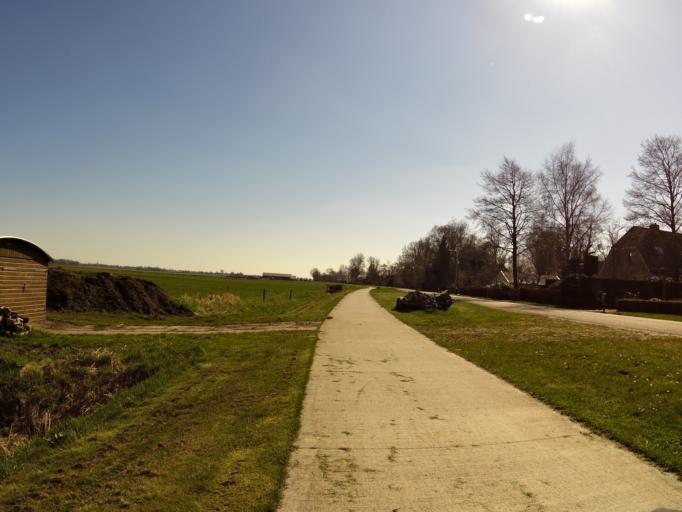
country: NL
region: Overijssel
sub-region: Gemeente Steenwijkerland
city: Blokzijl
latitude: 52.7657
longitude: 5.9919
